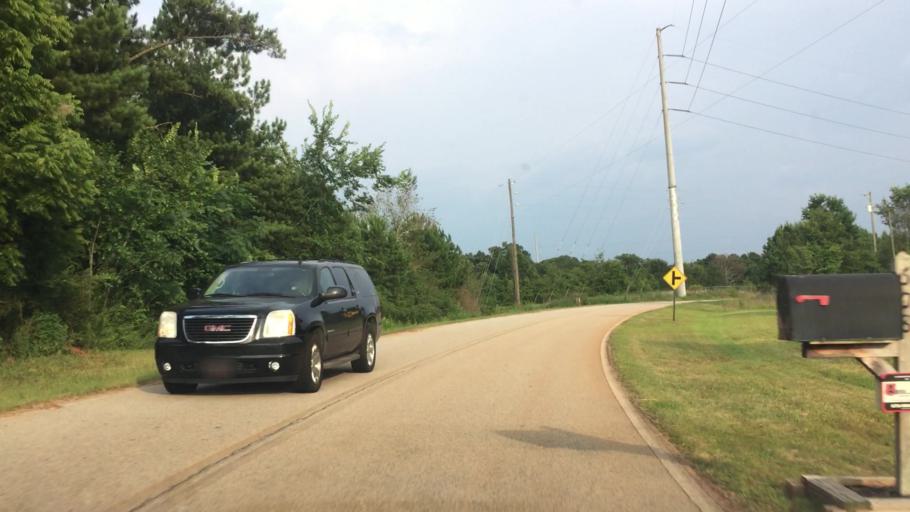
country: US
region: Georgia
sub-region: Henry County
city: McDonough
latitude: 33.5261
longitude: -84.1231
